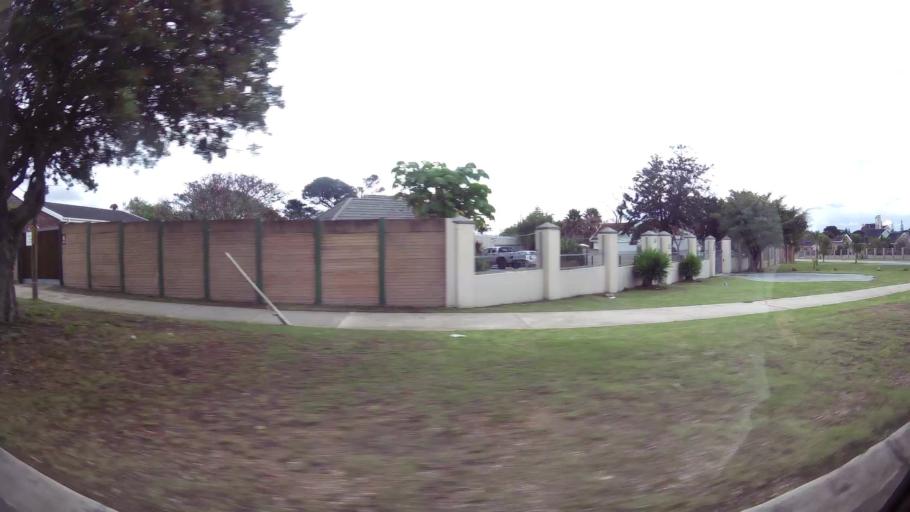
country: ZA
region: Eastern Cape
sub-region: Nelson Mandela Bay Metropolitan Municipality
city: Port Elizabeth
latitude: -33.9407
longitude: 25.5203
